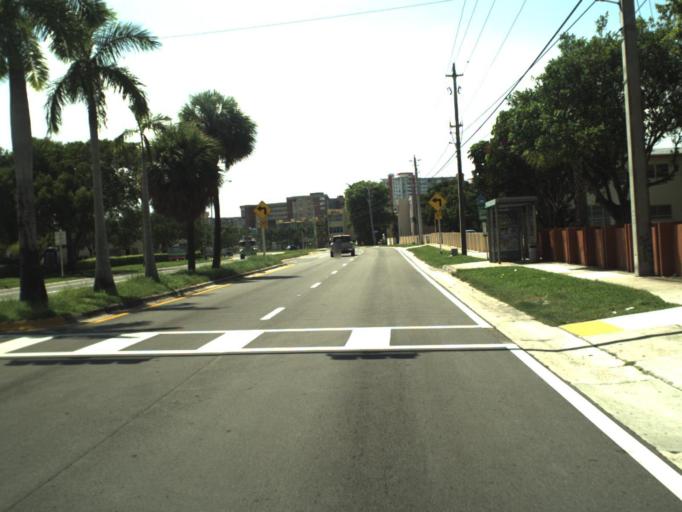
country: US
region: Florida
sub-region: Miami-Dade County
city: North Miami Beach
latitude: 25.9460
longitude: -80.1670
